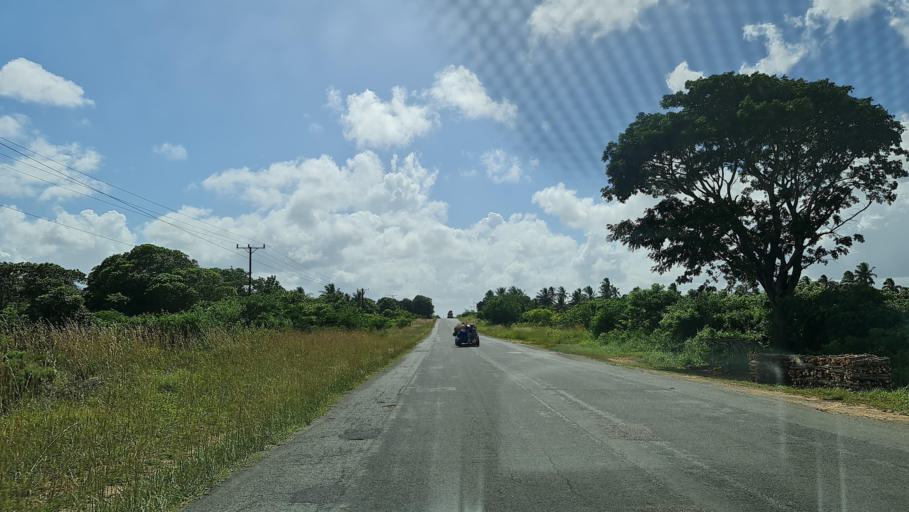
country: MZ
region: Gaza
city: Manjacaze
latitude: -24.6783
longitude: 34.5589
